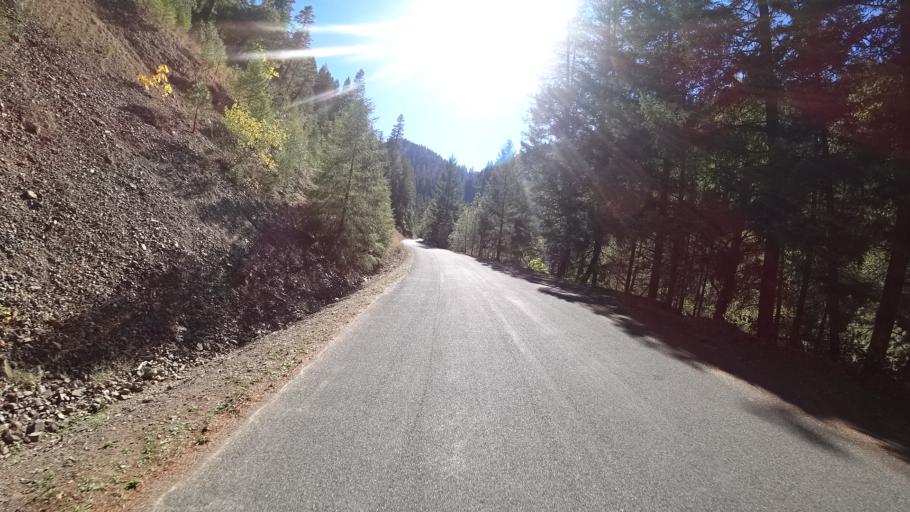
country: US
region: California
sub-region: Siskiyou County
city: Happy Camp
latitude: 41.3138
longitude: -123.1686
